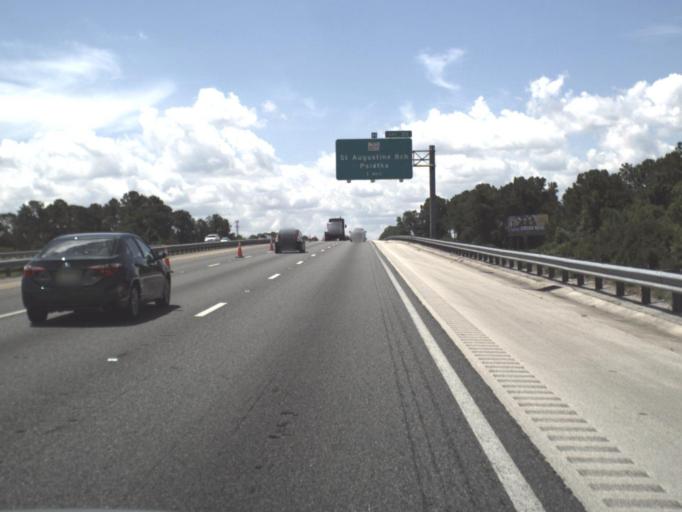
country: US
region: Florida
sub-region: Saint Johns County
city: Saint Augustine South
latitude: 29.8436
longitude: -81.3883
